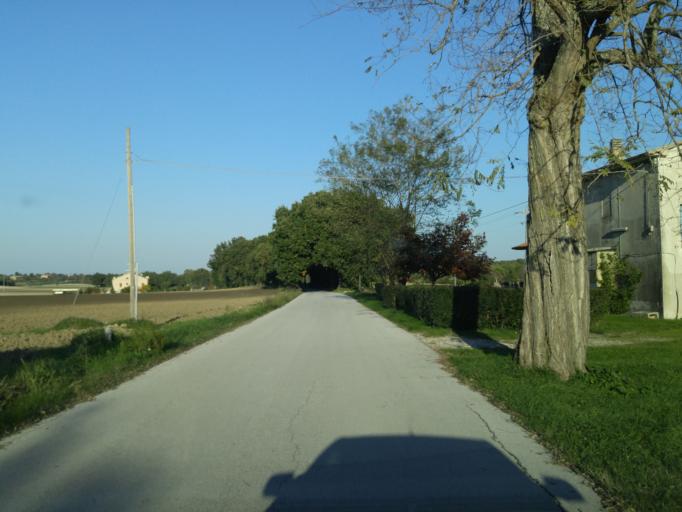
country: IT
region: The Marches
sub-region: Provincia di Pesaro e Urbino
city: Bellocchi
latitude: 43.8047
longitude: 13.0245
